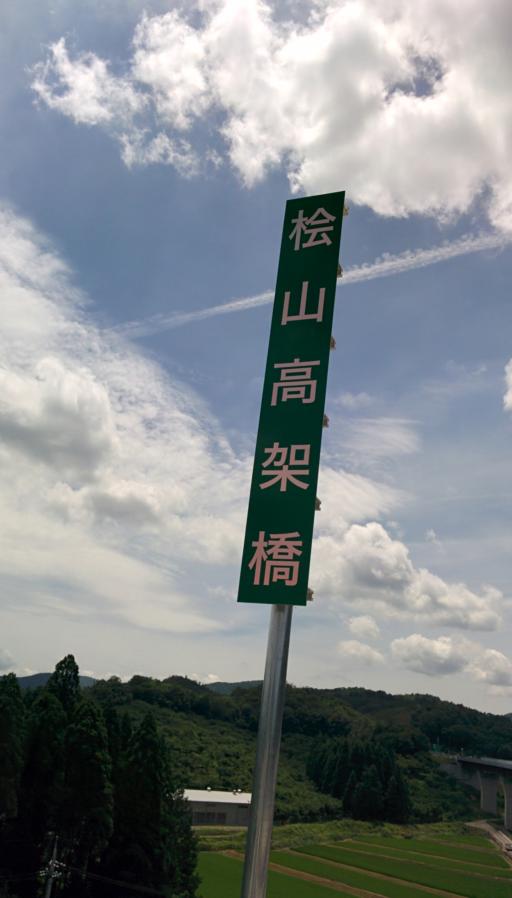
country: JP
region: Kyoto
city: Ayabe
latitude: 35.1742
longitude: 135.3688
